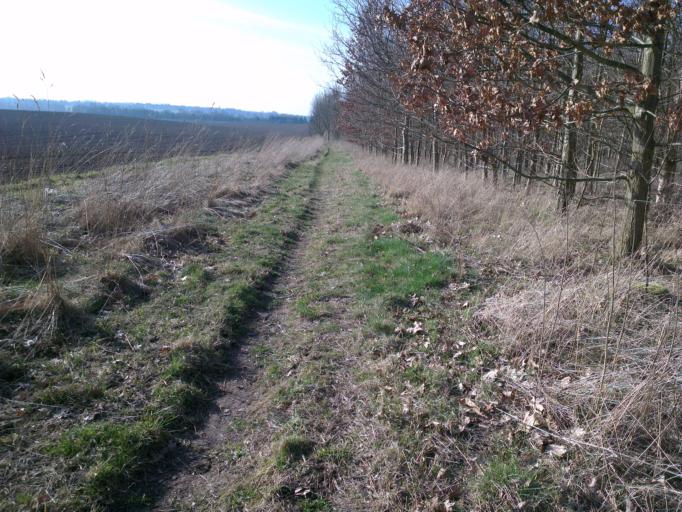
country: DK
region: Capital Region
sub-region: Frederikssund Kommune
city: Frederikssund
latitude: 55.8399
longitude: 12.0936
